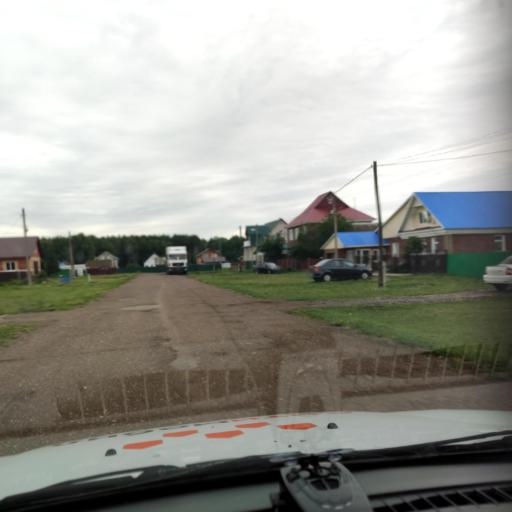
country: RU
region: Bashkortostan
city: Kabakovo
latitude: 54.4558
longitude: 55.9541
